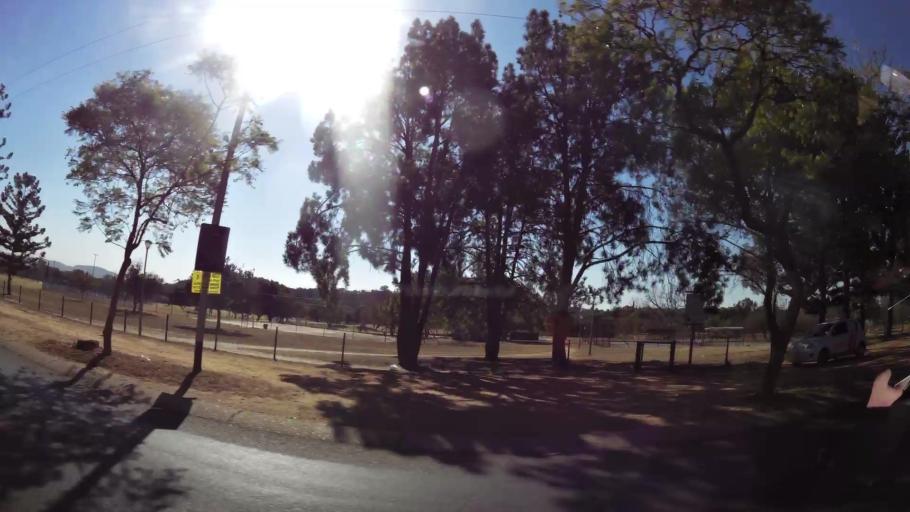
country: ZA
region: Gauteng
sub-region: City of Tshwane Metropolitan Municipality
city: Pretoria
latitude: -25.7337
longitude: 28.2253
